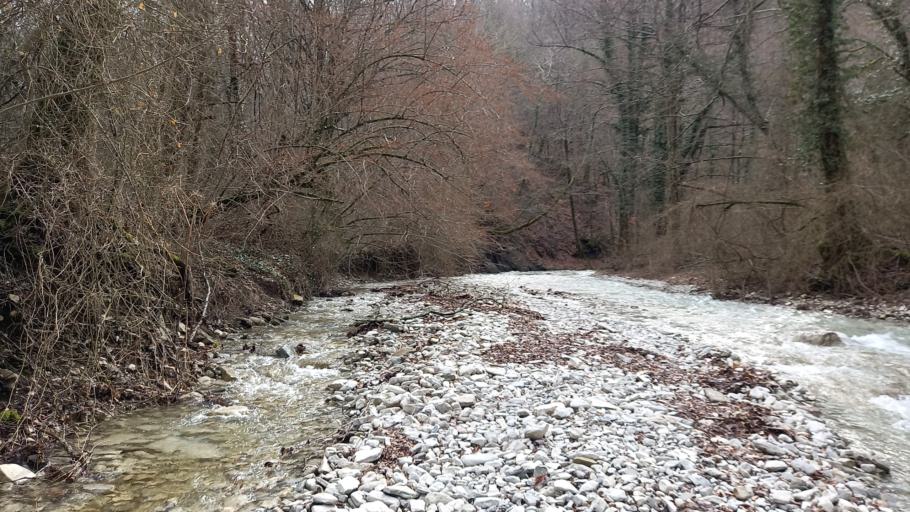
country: RU
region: Krasnodarskiy
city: Dzhubga
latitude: 44.4083
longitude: 38.7147
